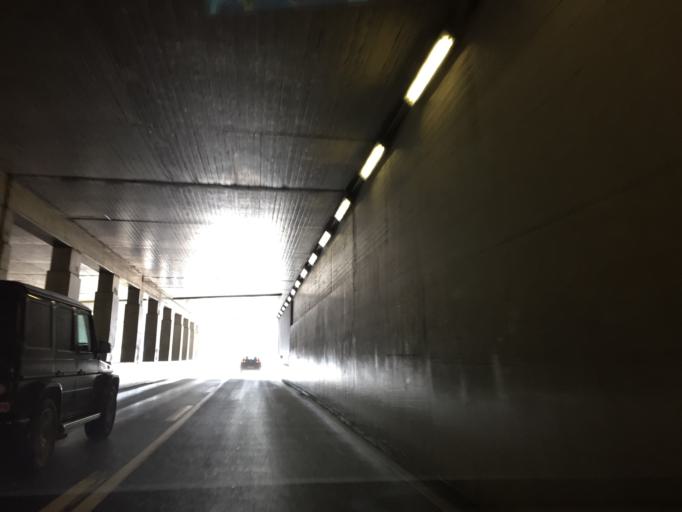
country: CH
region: Schwyz
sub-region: Bezirk Hoefe
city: Schindellegi
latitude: 47.1749
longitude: 8.7122
